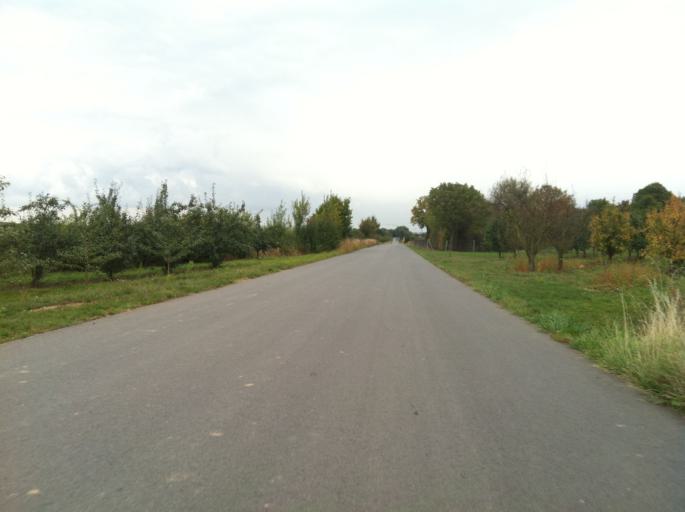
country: DE
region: Rheinland-Pfalz
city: Wackernheim
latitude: 49.9617
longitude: 8.1332
